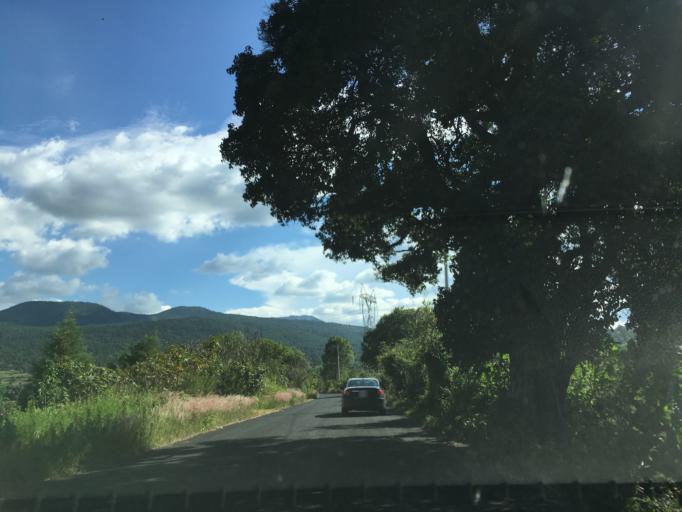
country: MX
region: Michoacan
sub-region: Zacapu
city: Naranja de Tapia
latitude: 19.7737
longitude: -101.7667
